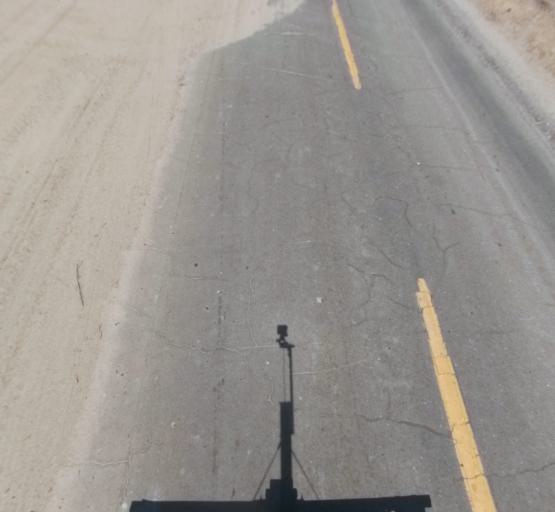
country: US
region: California
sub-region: Fresno County
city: Biola
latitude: 36.8416
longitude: -120.1103
